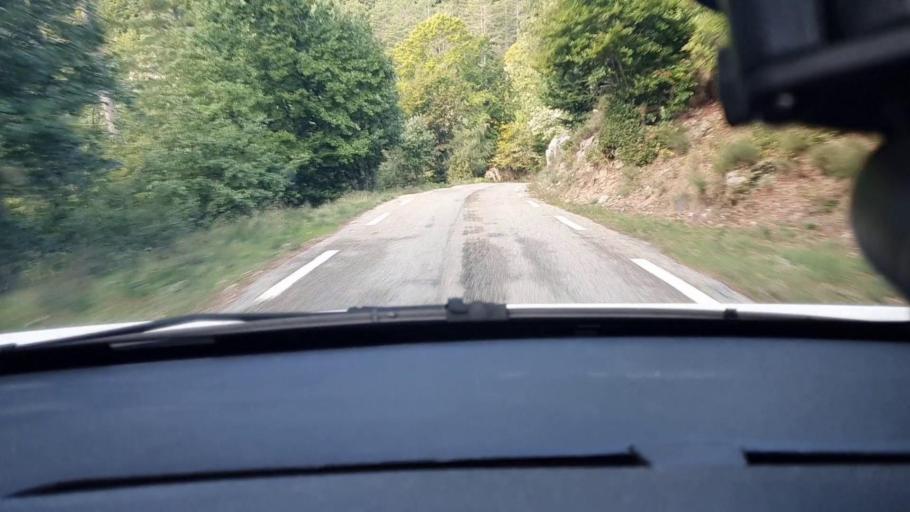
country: FR
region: Languedoc-Roussillon
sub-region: Departement du Gard
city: Branoux-les-Taillades
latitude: 44.3694
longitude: 3.9229
